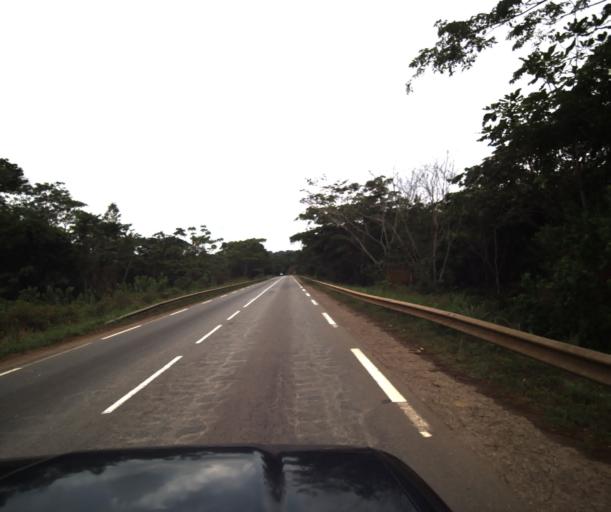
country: CM
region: Centre
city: Eseka
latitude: 3.8293
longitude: 10.9988
